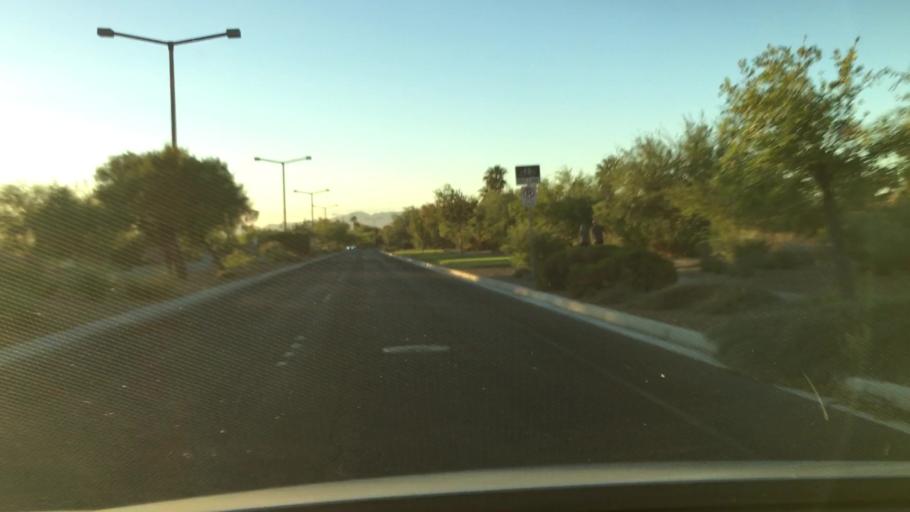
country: US
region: Nevada
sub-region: Clark County
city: Summerlin South
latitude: 36.1256
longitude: -115.3392
